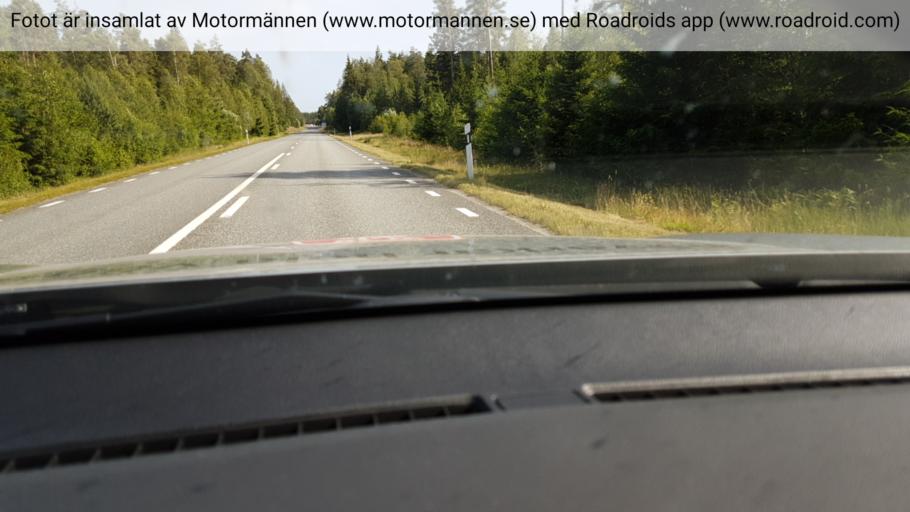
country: SE
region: Joenkoeping
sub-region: Vetlanda Kommun
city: Ekenassjon
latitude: 57.5634
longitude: 14.9761
